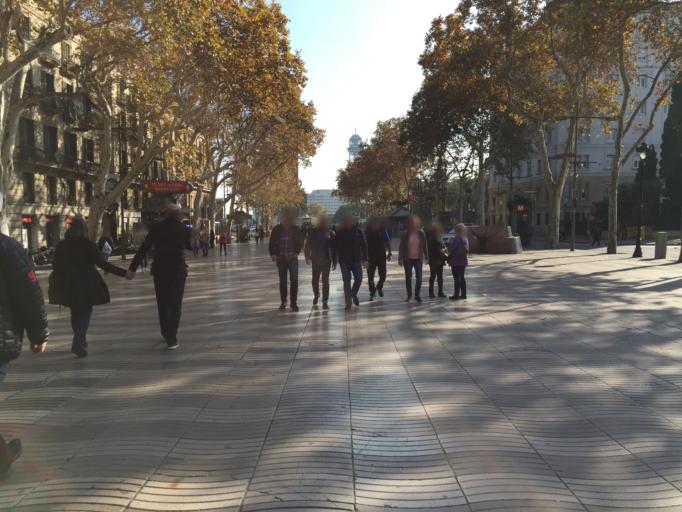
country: ES
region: Catalonia
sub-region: Provincia de Barcelona
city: Ciutat Vella
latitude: 41.3775
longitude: 2.1762
